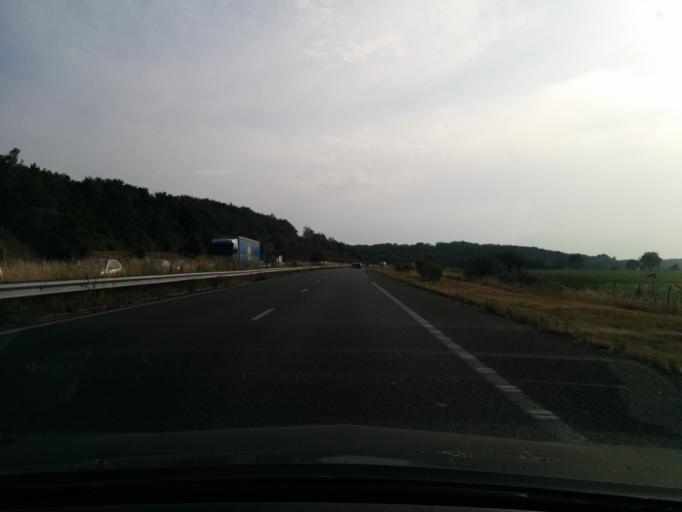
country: FR
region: Midi-Pyrenees
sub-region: Departement de la Haute-Garonne
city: Buzet-sur-Tarn
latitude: 43.7488
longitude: 1.6392
